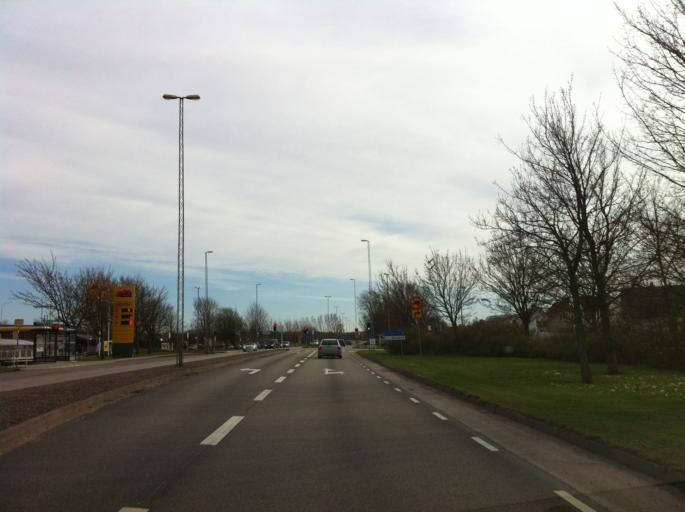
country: SE
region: Skane
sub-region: Hoganas Kommun
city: Hoganas
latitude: 56.1969
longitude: 12.5636
